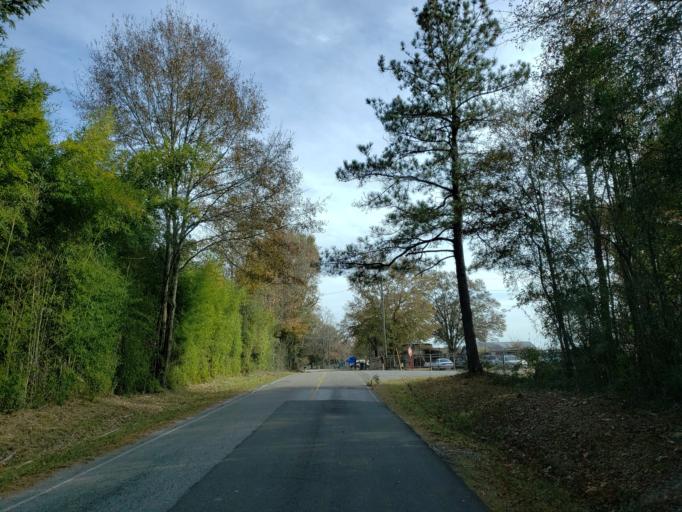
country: US
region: Mississippi
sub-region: Forrest County
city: Rawls Springs
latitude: 31.4013
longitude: -89.3949
